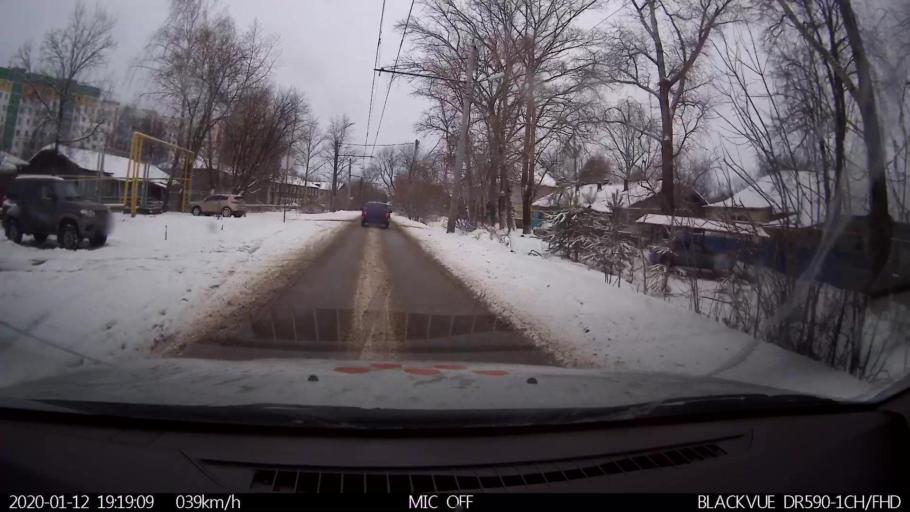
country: RU
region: Nizjnij Novgorod
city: Nizhniy Novgorod
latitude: 56.2906
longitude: 43.9085
